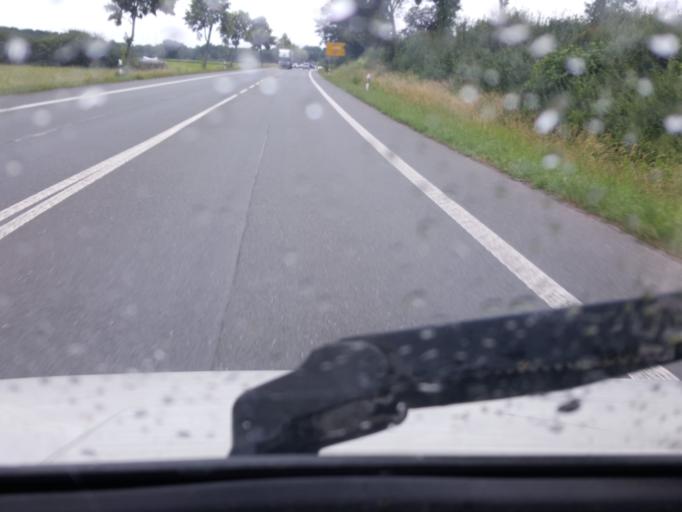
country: DE
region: North Rhine-Westphalia
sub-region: Regierungsbezirk Detmold
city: Petershagen
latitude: 52.3724
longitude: 8.9550
